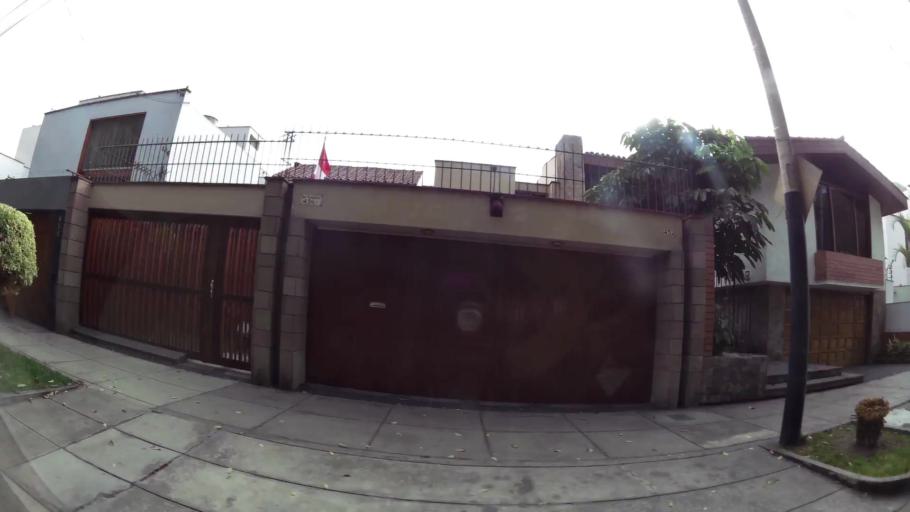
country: PE
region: Lima
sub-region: Lima
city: San Isidro
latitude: -12.0997
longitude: -77.0524
